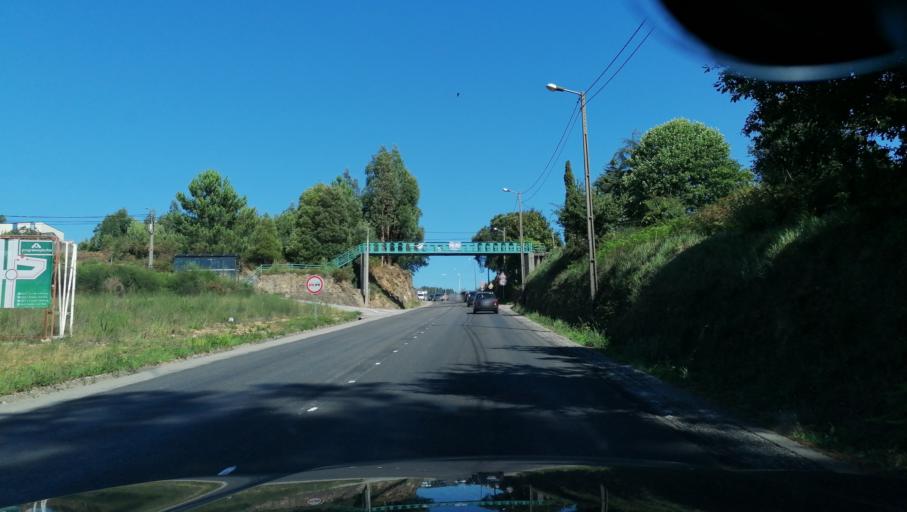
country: PT
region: Aveiro
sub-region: Santa Maria da Feira
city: Feira
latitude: 40.9305
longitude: -8.5196
